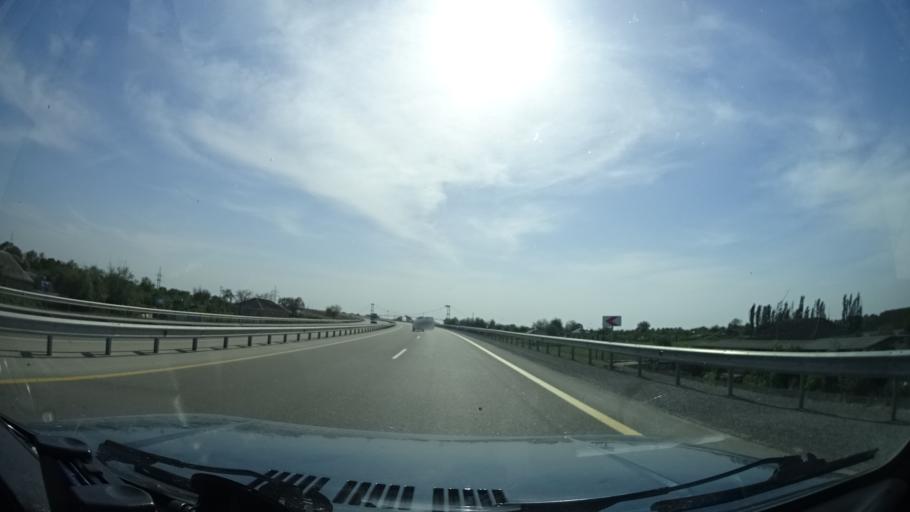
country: AZ
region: Salyan
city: Salyan
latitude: 39.6345
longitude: 48.9708
